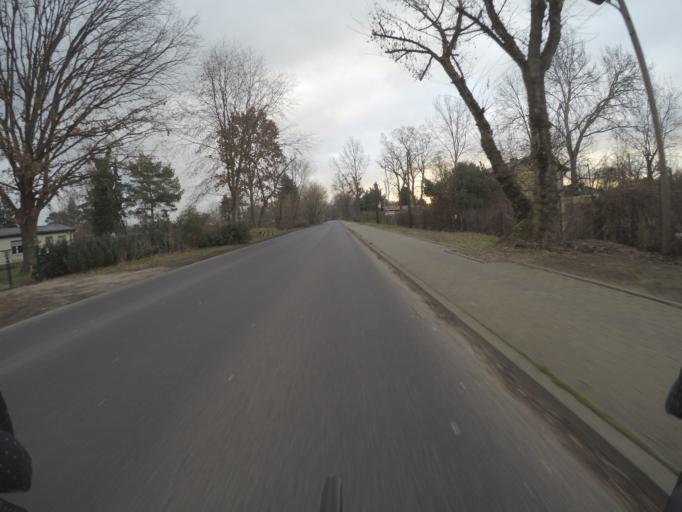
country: DE
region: Berlin
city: Karlshorst
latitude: 52.4757
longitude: 13.5401
